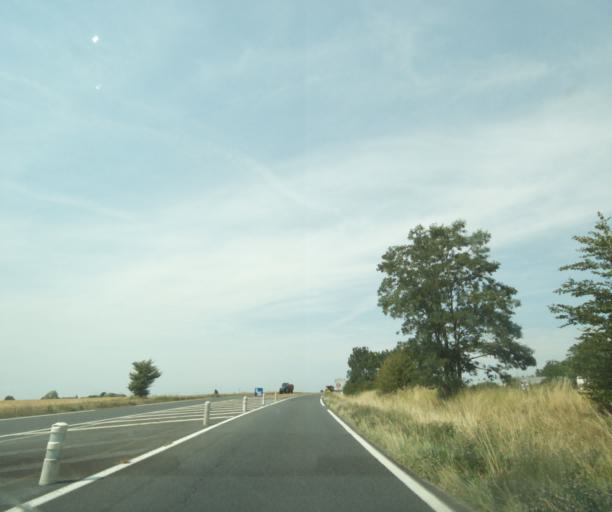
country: FR
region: Centre
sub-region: Departement d'Indre-et-Loire
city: Sainte-Maure-de-Touraine
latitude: 47.1560
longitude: 0.6461
